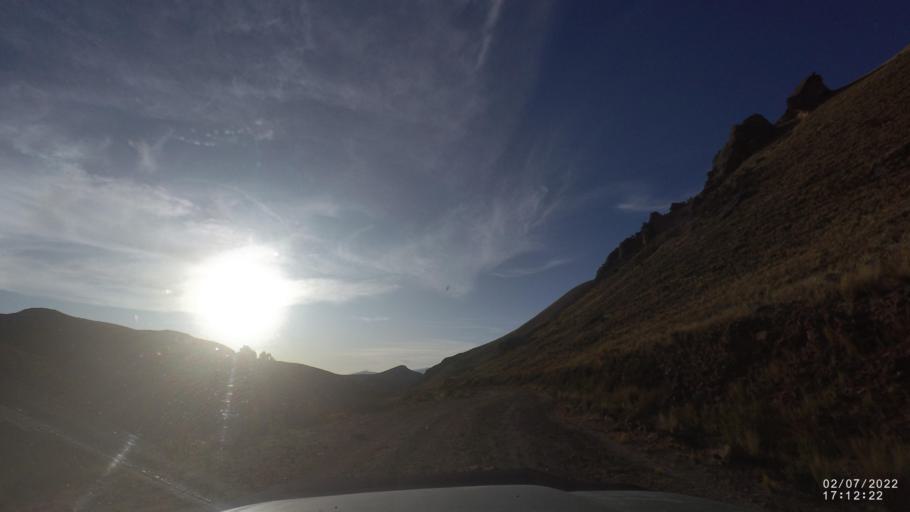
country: BO
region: Cochabamba
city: Irpa Irpa
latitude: -17.8856
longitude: -66.5702
